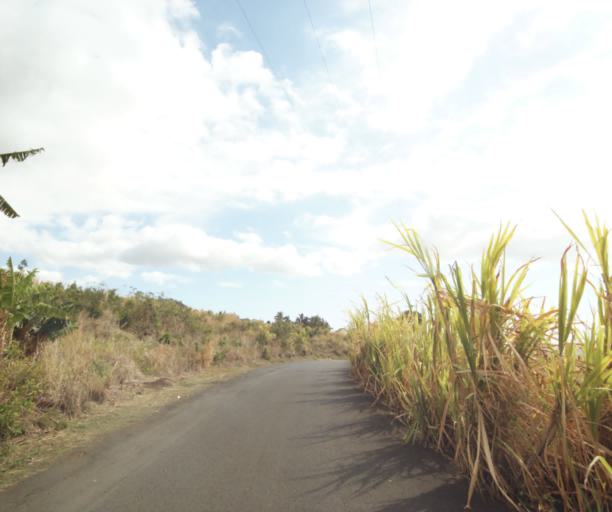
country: RE
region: Reunion
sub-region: Reunion
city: Saint-Paul
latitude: -21.0295
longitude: 55.2874
